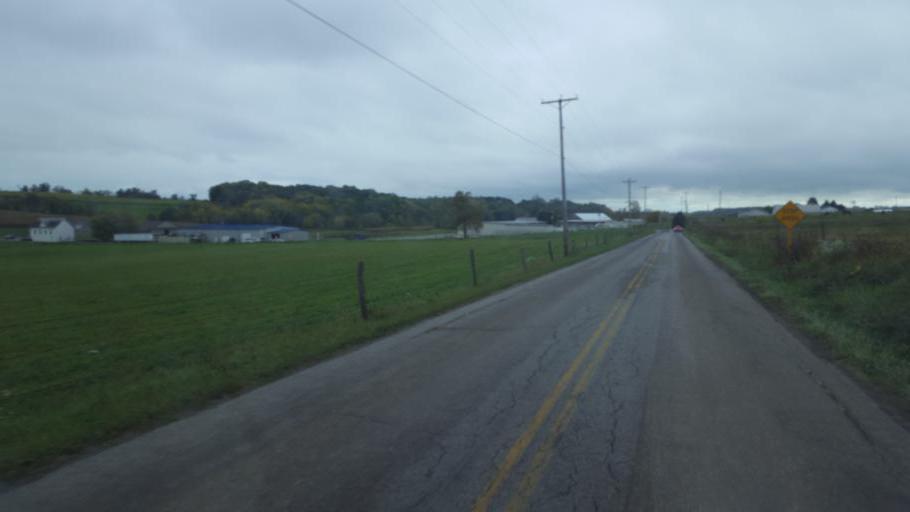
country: US
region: Ohio
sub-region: Holmes County
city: Millersburg
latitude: 40.6259
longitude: -81.8130
